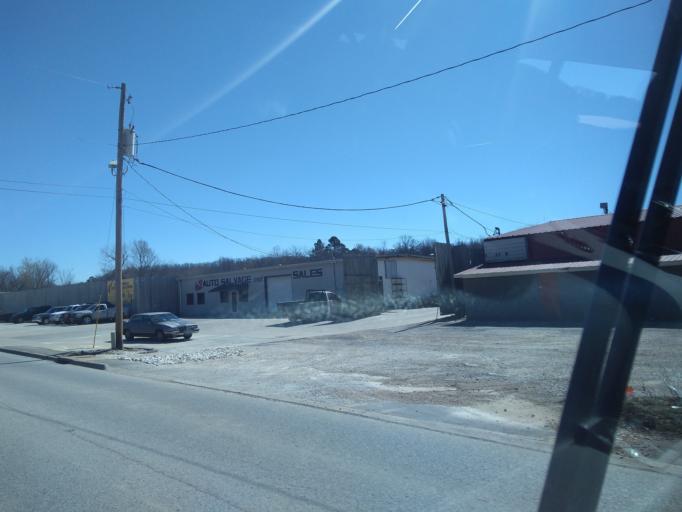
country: US
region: Arkansas
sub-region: Washington County
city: Farmington
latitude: 36.0495
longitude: -94.2130
